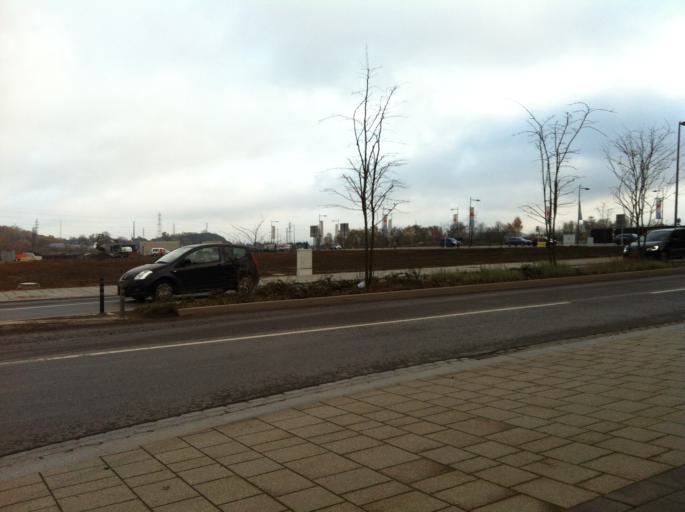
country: LU
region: Luxembourg
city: Belvaux
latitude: 49.5051
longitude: 5.9468
